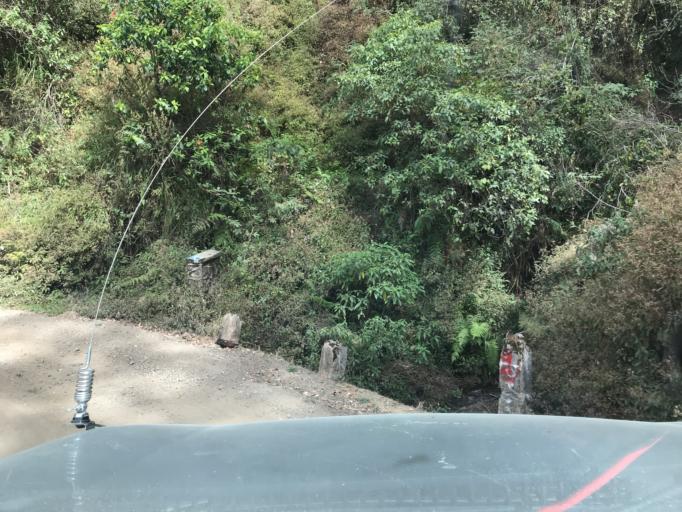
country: TL
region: Ainaro
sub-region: Ainaro
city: Ainaro
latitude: -8.8810
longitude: 125.5424
